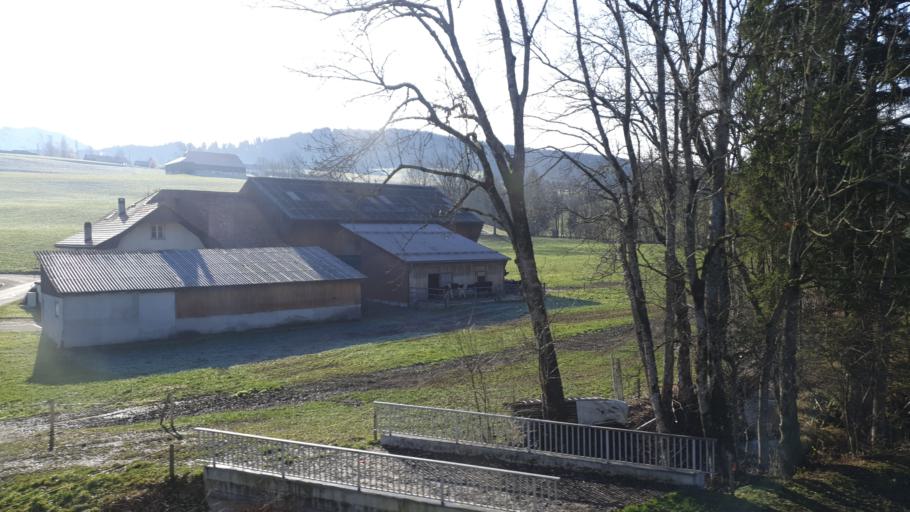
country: CH
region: Fribourg
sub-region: Gruyere District
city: Vuadens
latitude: 46.6174
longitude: 6.9997
